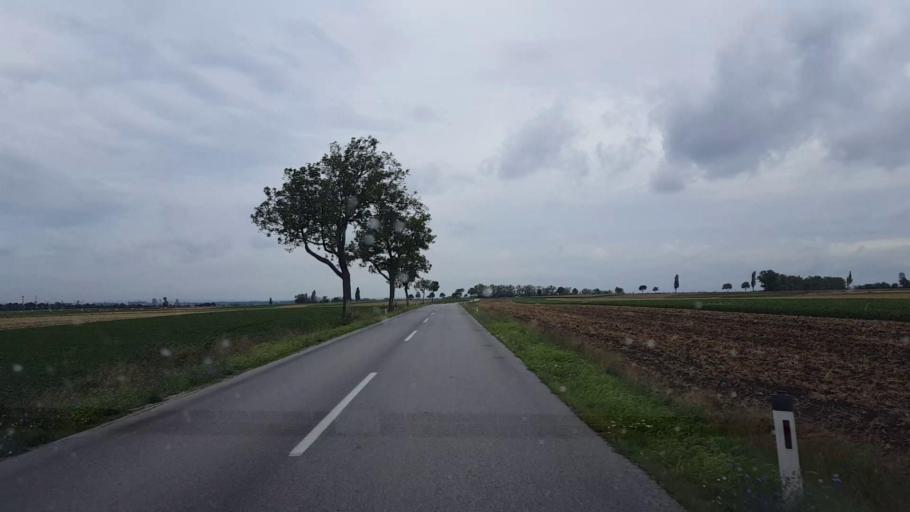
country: AT
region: Lower Austria
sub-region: Politischer Bezirk Wien-Umgebung
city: Rauchenwarth
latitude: 48.0995
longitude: 16.5269
